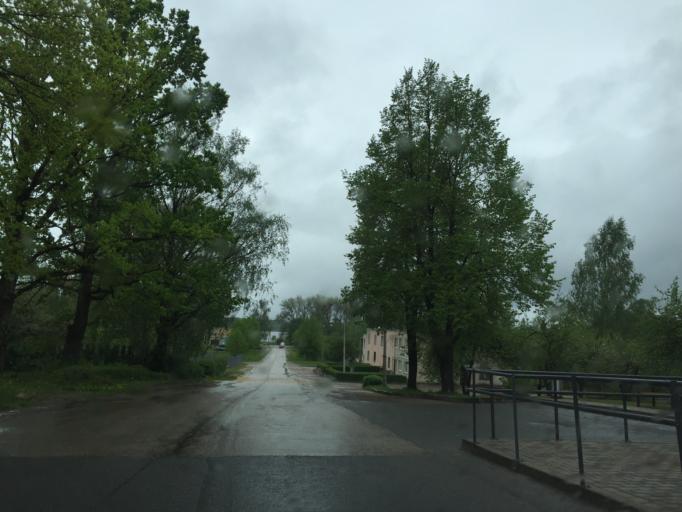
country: LV
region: Lielvarde
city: Lielvarde
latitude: 56.7234
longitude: 24.7868
